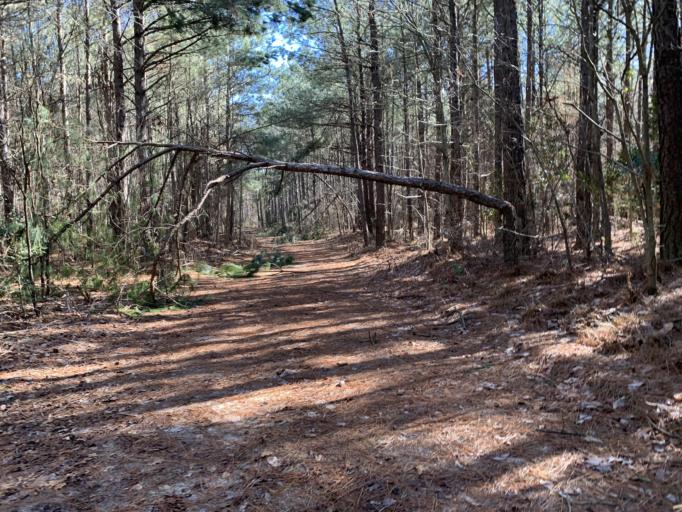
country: US
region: Delaware
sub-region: Sussex County
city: Georgetown
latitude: 38.6753
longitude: -75.4839
